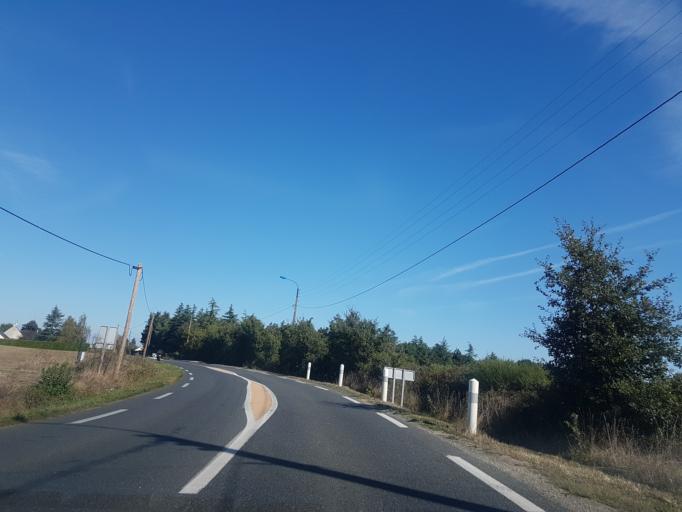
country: FR
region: Pays de la Loire
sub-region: Departement de la Loire-Atlantique
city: Nort-sur-Erdre
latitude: 47.4259
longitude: -1.4815
